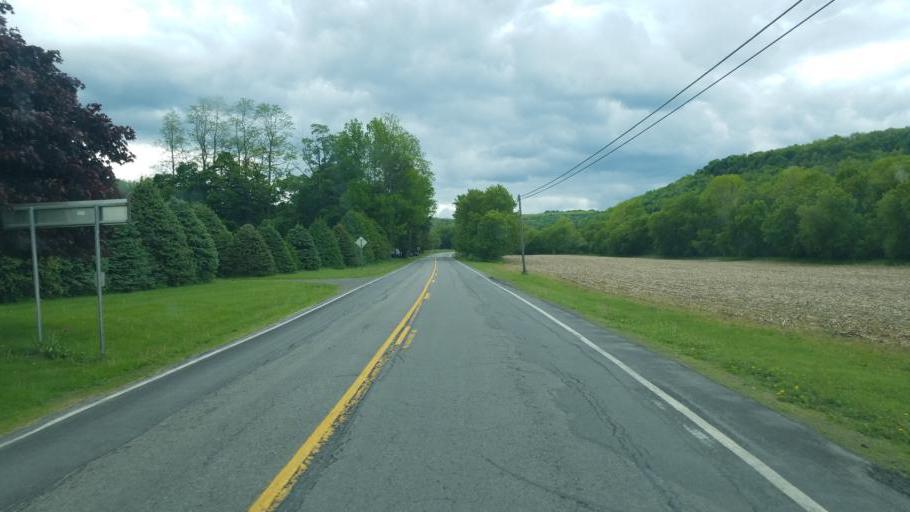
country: US
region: New York
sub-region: Oneida County
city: Chadwicks
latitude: 42.8616
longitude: -75.1911
